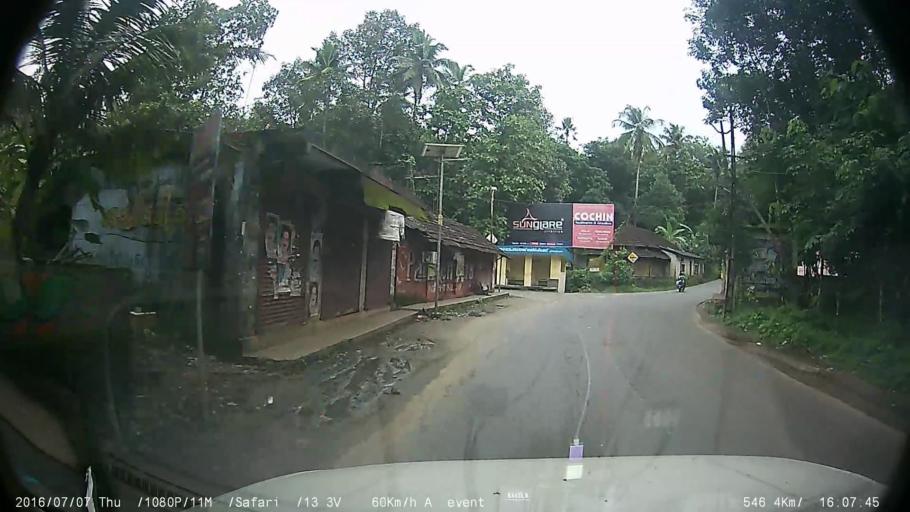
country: IN
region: Kerala
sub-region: Kottayam
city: Palackattumala
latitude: 9.8042
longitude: 76.6138
